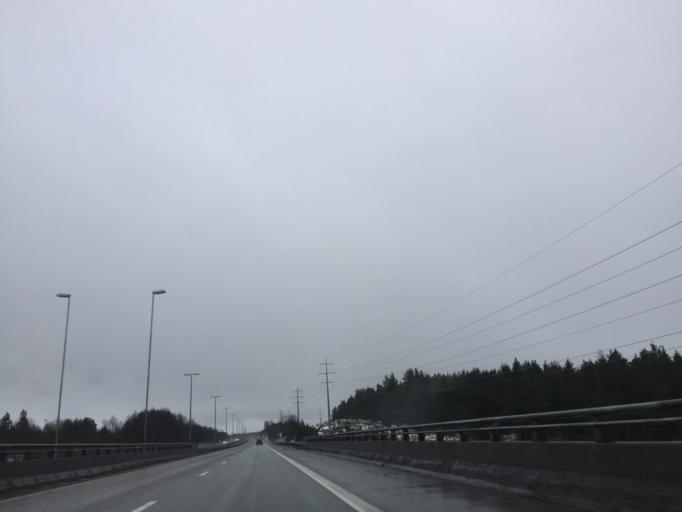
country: NO
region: Akershus
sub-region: Vestby
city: Vestby
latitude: 59.5562
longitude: 10.7215
